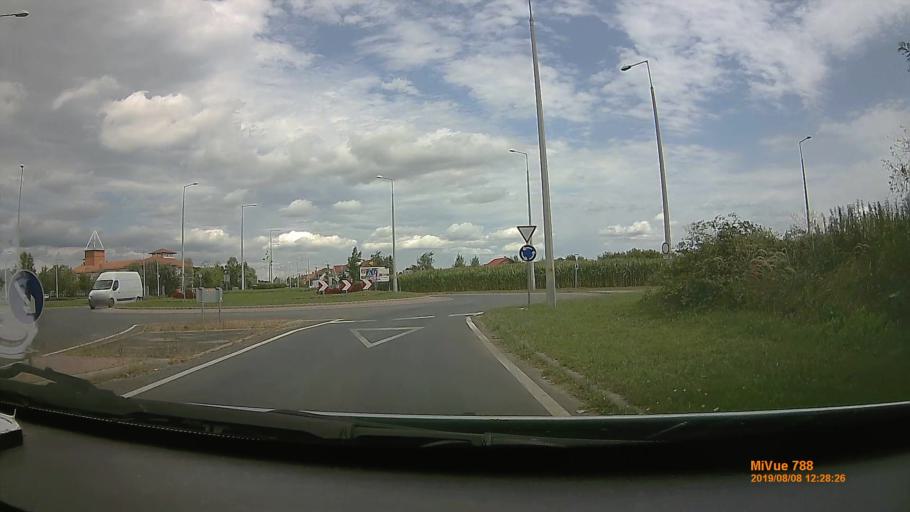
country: HU
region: Szabolcs-Szatmar-Bereg
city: Nyirbator
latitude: 47.8296
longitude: 22.1127
